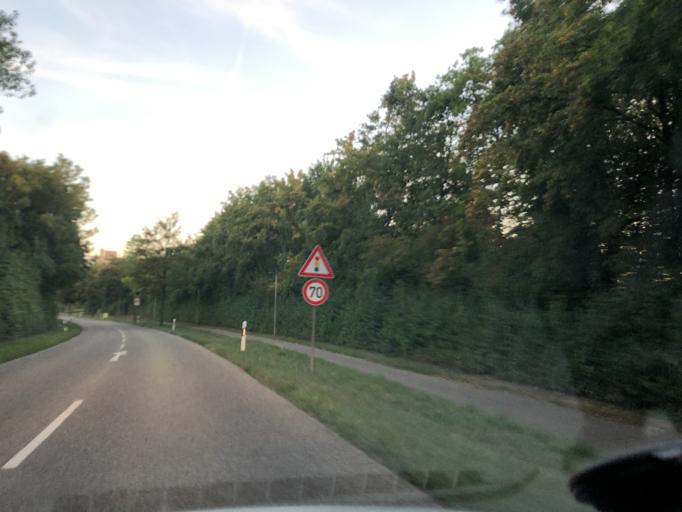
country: DE
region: Baden-Wuerttemberg
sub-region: Regierungsbezirk Stuttgart
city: Erdmannhausen
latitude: 48.8784
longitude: 9.2804
